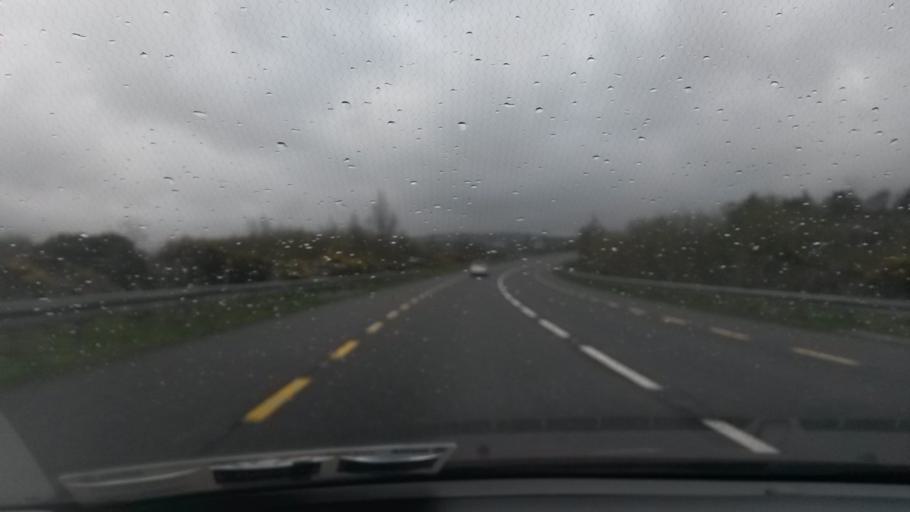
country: IE
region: Munster
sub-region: County Limerick
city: Abbeyfeale
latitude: 52.3147
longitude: -9.3606
